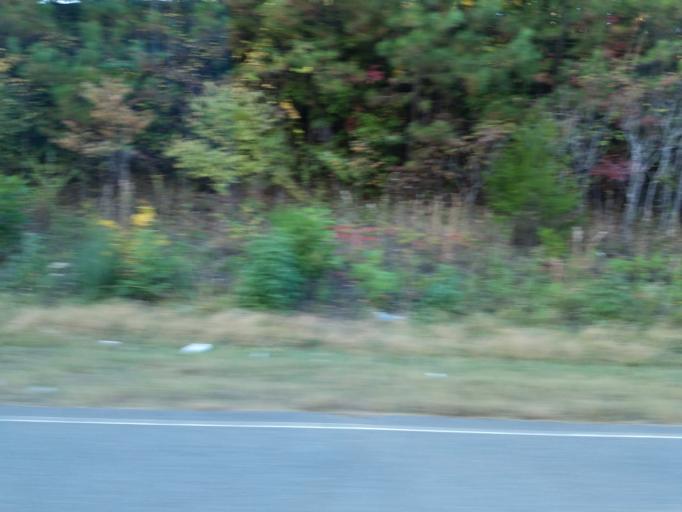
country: US
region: Georgia
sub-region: Bartow County
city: Adairsville
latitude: 34.2777
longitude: -84.9487
